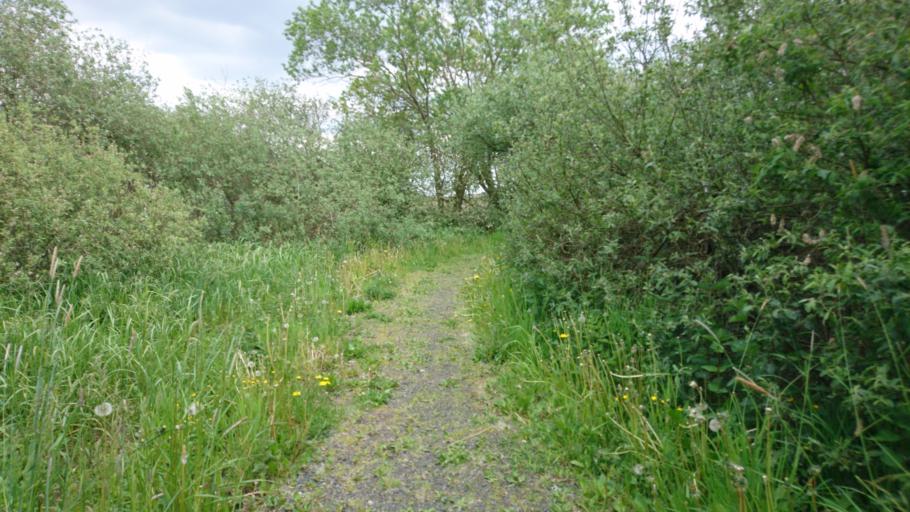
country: SE
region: Skane
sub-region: Kristianstads Kommun
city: Fjalkinge
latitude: 56.0028
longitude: 14.2415
